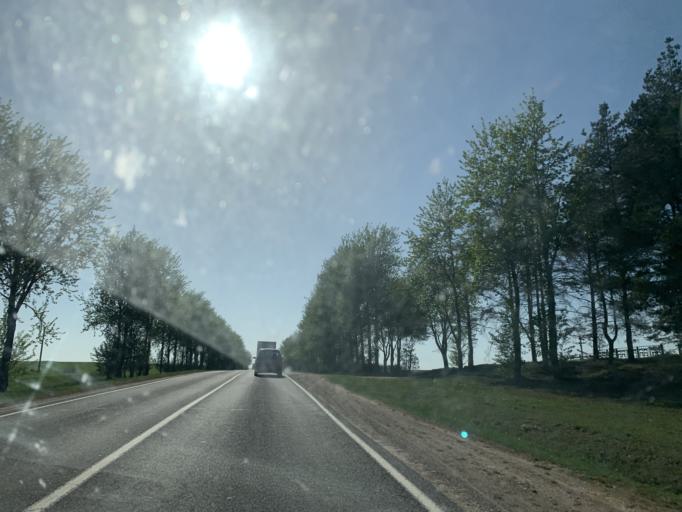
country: BY
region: Minsk
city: Nyasvizh
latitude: 53.2339
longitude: 26.8089
